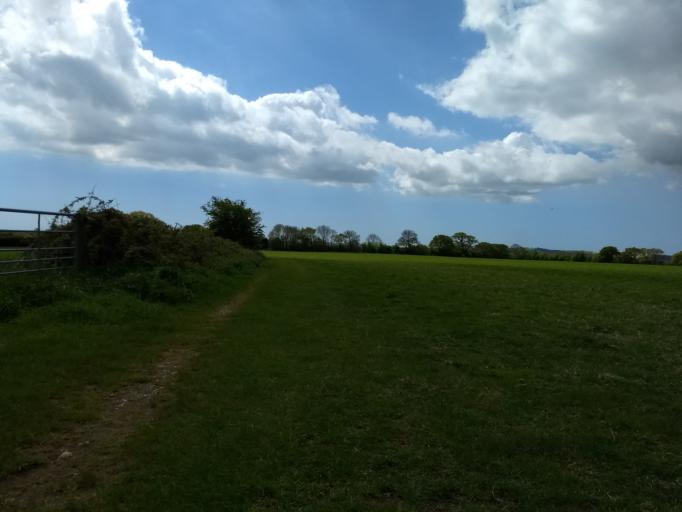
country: GB
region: England
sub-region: Isle of Wight
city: Seaview
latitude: 50.7060
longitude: -1.1107
